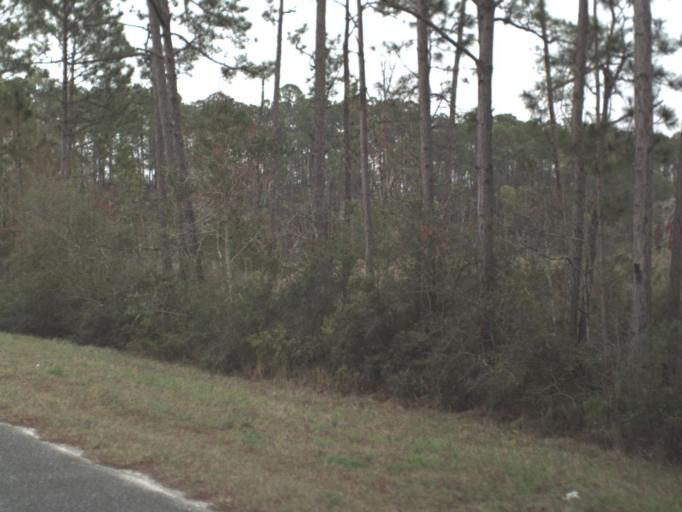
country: US
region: Florida
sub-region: Franklin County
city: Eastpoint
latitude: 29.8293
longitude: -84.8851
